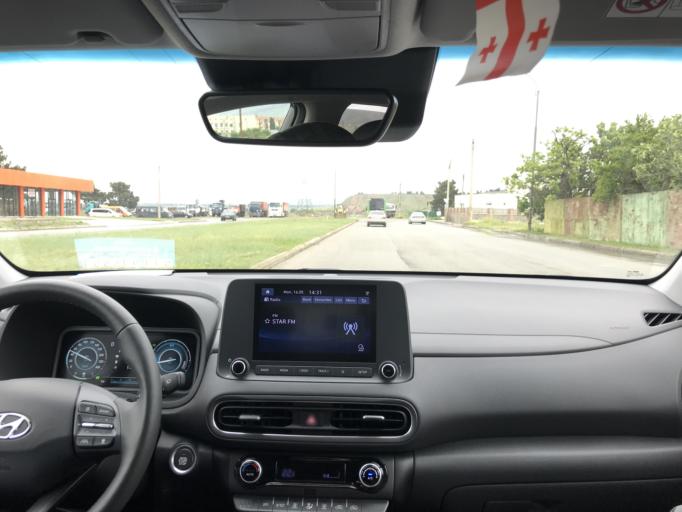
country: GE
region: Kvemo Kartli
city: Rust'avi
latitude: 41.5673
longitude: 44.9983
